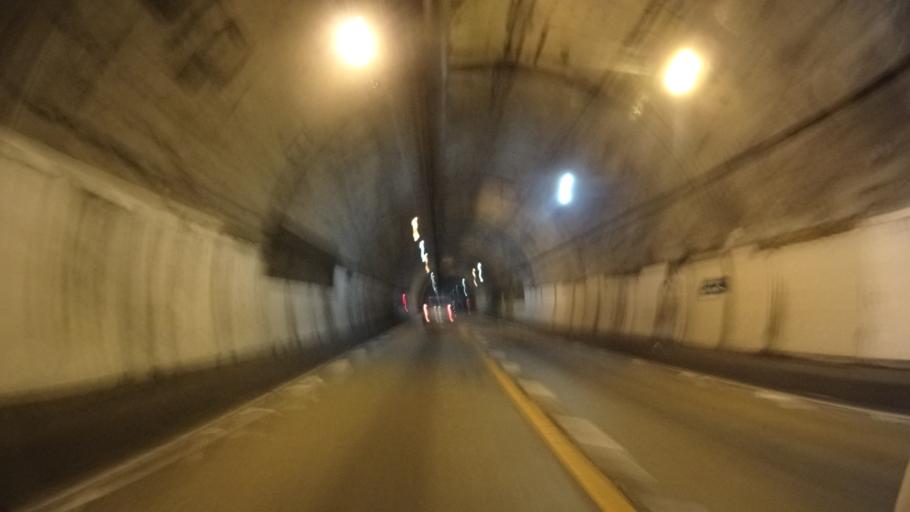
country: JP
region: Shimane
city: Masuda
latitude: 34.6699
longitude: 131.7134
